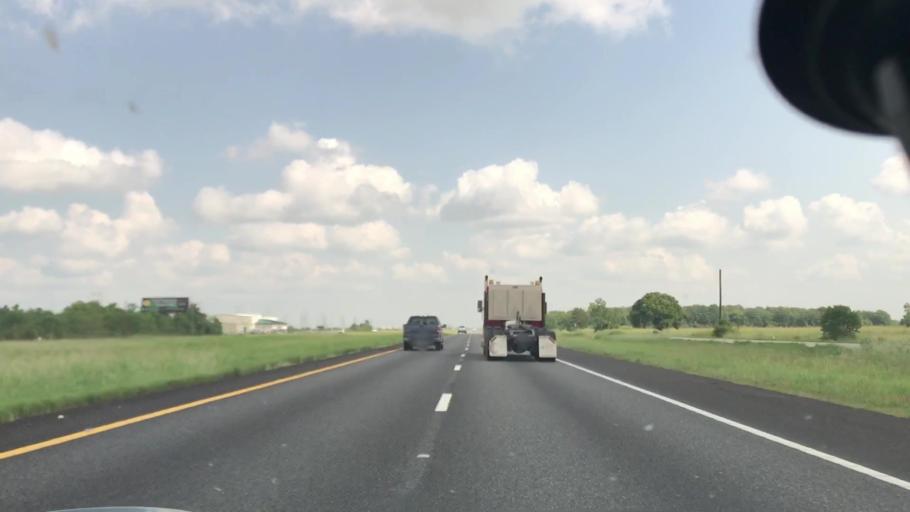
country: US
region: Texas
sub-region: Brazoria County
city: Rosharon
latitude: 29.3997
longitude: -95.4267
